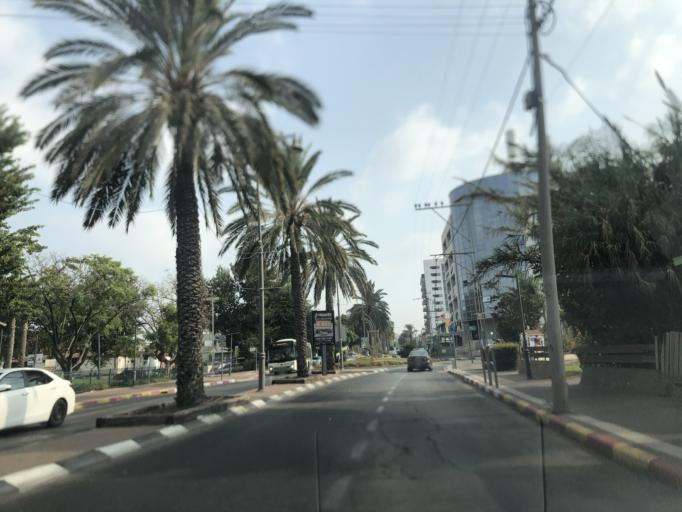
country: IL
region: Central District
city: Rosh Ha'Ayin
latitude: 32.0975
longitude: 34.9428
